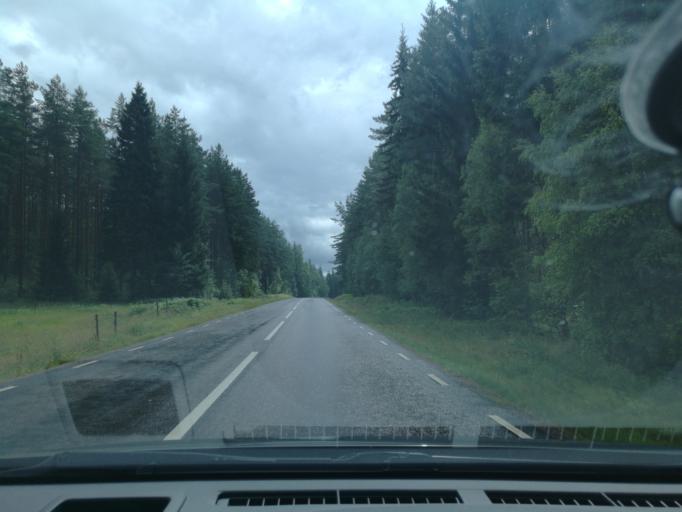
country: SE
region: OEstergoetland
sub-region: Motala Kommun
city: Borensberg
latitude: 58.7408
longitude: 15.3713
